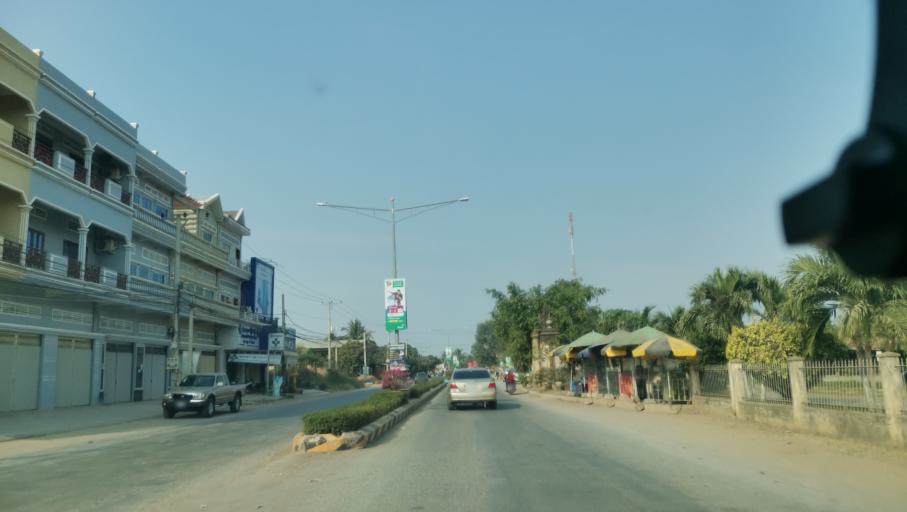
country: KH
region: Battambang
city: Battambang
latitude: 13.0843
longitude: 103.1909
